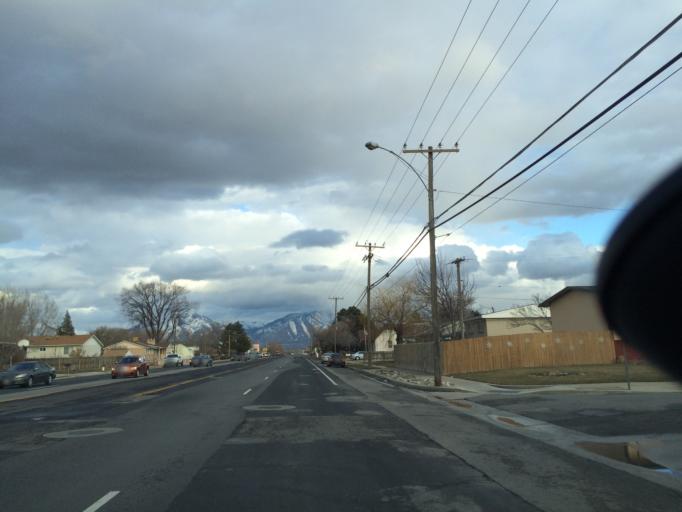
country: US
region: Utah
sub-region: Salt Lake County
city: Taylorsville
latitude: 40.6821
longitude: -111.9468
